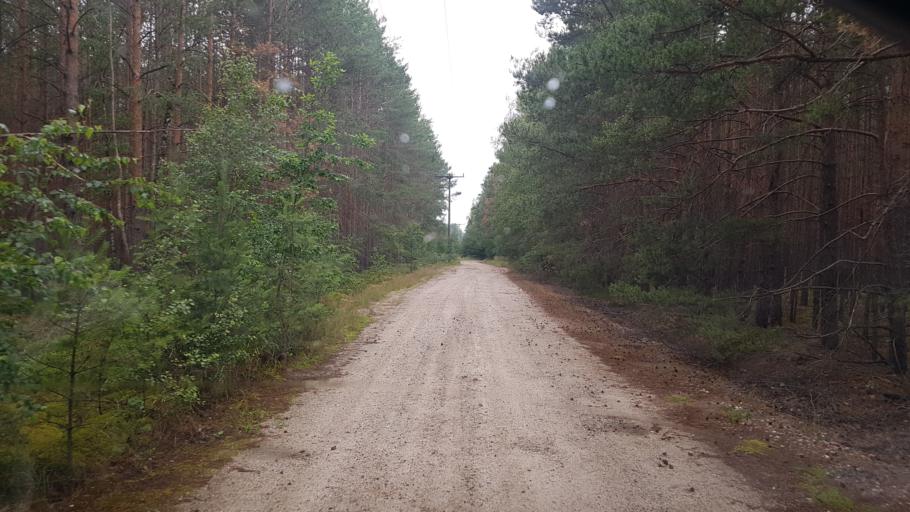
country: DE
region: Brandenburg
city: Finsterwalde
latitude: 51.5899
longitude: 13.7264
